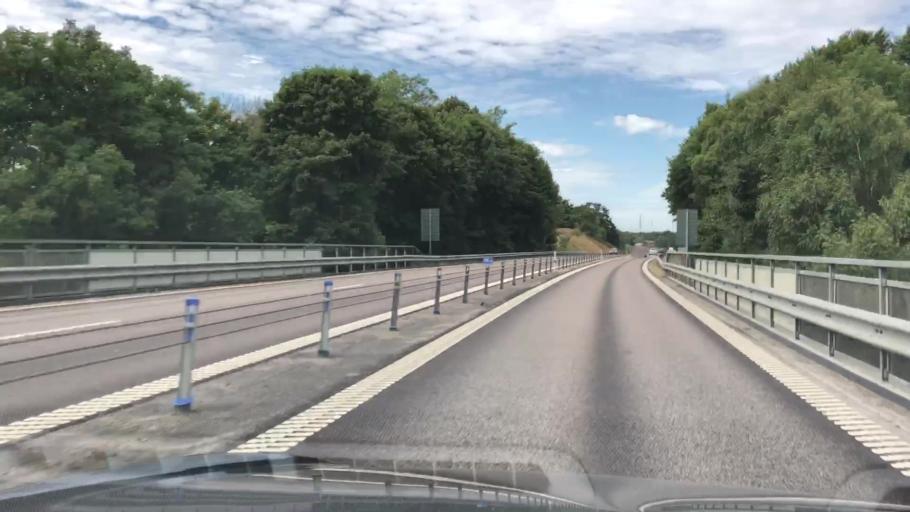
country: SE
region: Blekinge
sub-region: Karlskrona Kommun
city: Rodeby
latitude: 56.2033
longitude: 15.6563
